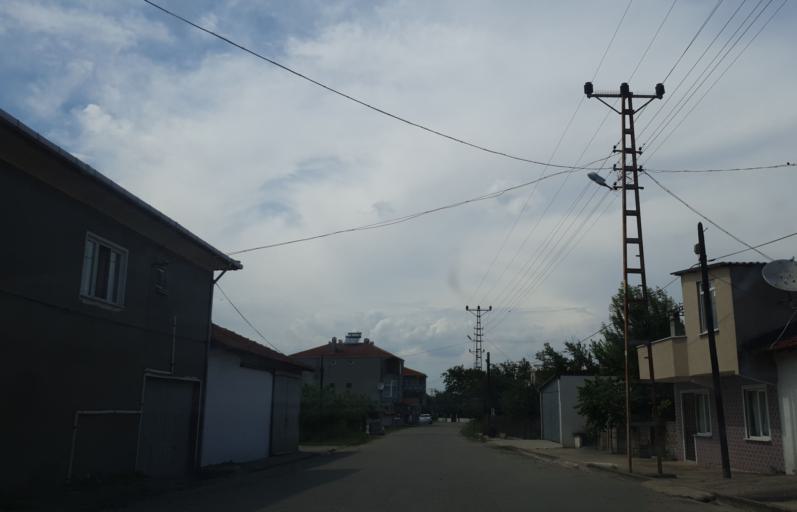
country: TR
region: Tekirdag
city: Muratli
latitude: 41.2187
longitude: 27.5476
